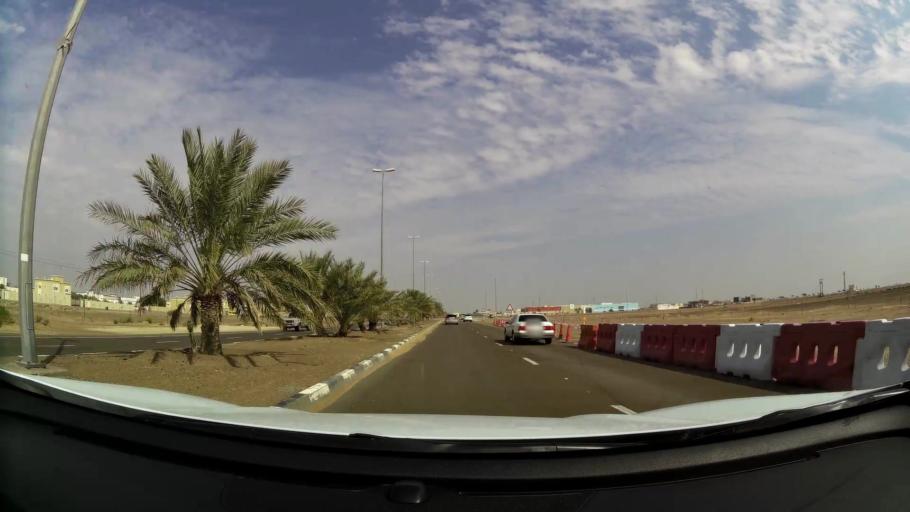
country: AE
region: Abu Dhabi
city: Al Ain
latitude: 24.0929
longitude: 55.8904
